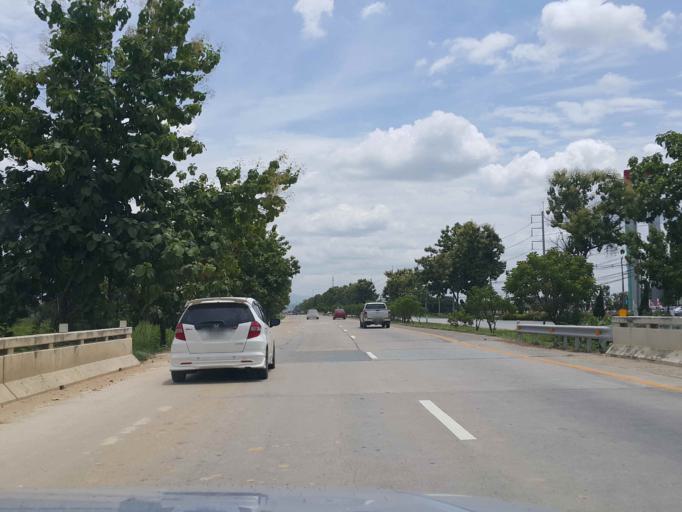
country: TH
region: Lamphun
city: Lamphun
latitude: 18.6073
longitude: 99.0436
